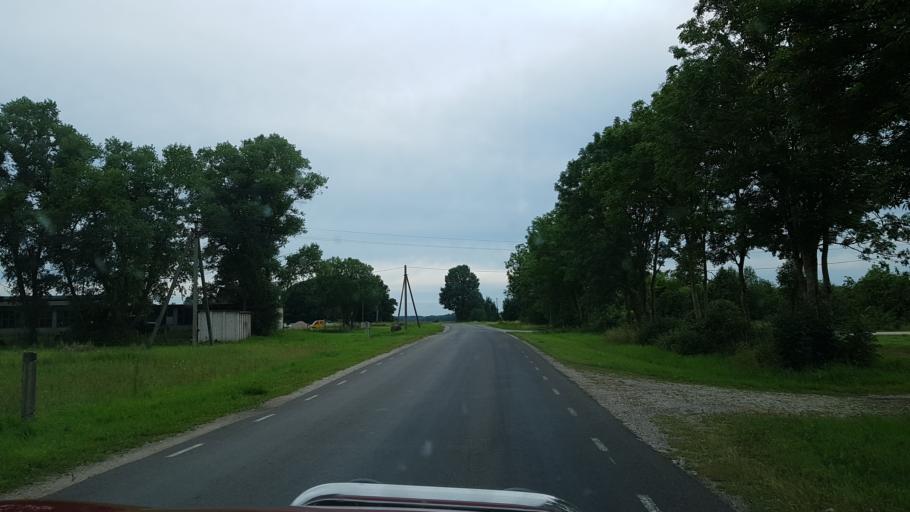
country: EE
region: Laeaene
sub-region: Lihula vald
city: Lihula
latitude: 58.8530
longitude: 23.7971
